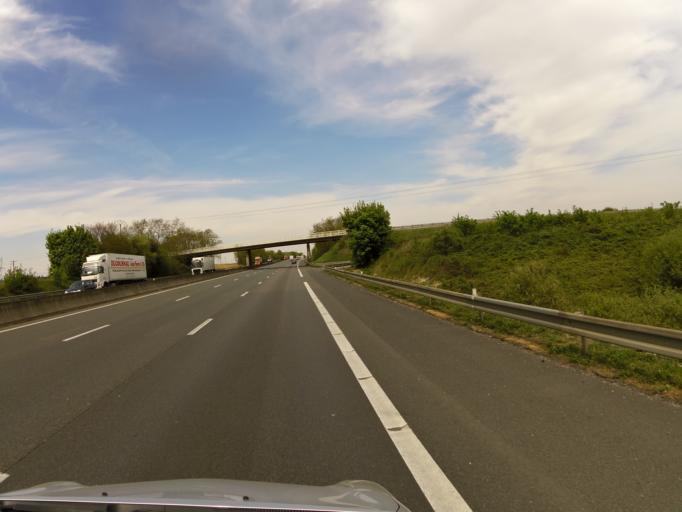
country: FR
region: Centre
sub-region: Departement du Loiret
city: Chevilly
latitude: 48.0438
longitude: 1.8407
